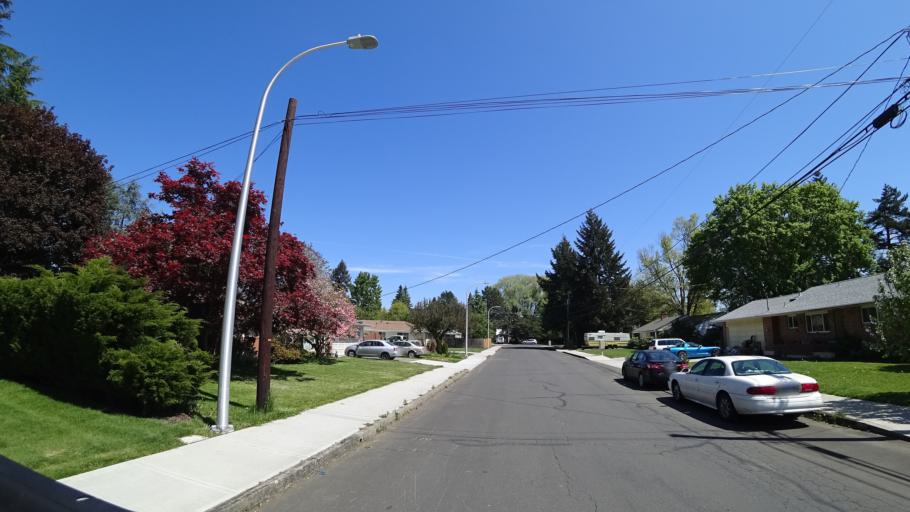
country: US
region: Oregon
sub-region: Washington County
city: Hillsboro
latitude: 45.5133
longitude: -122.9625
